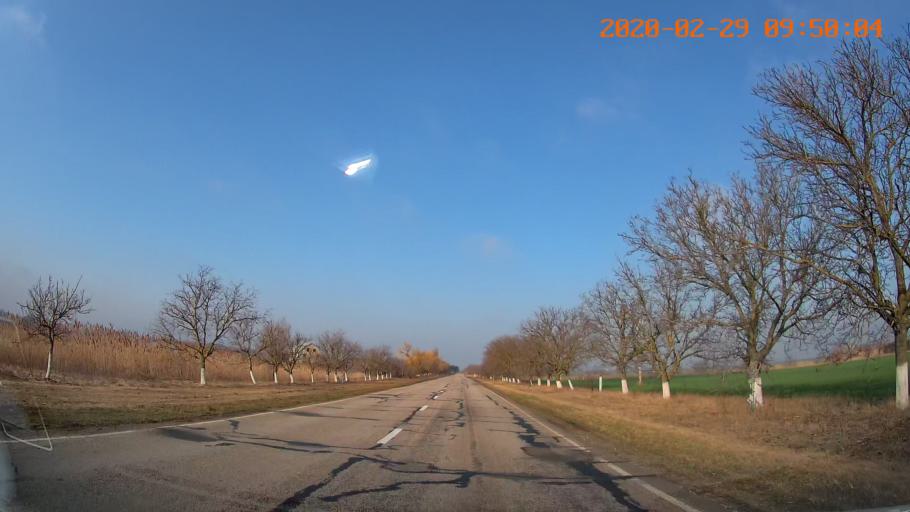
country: MD
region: Telenesti
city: Slobozia
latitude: 46.7010
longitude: 29.7624
